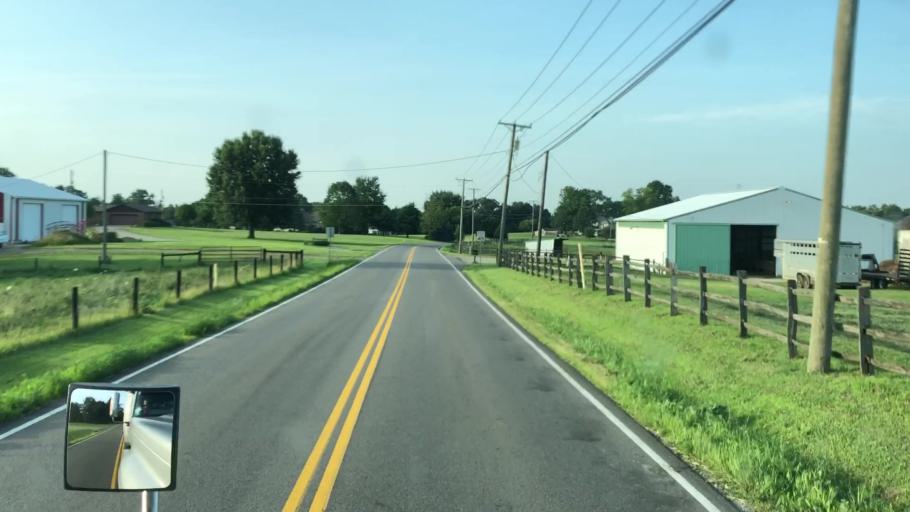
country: US
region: Ohio
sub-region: Muskingum County
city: Pleasant Grove
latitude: 39.9692
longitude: -81.9549
